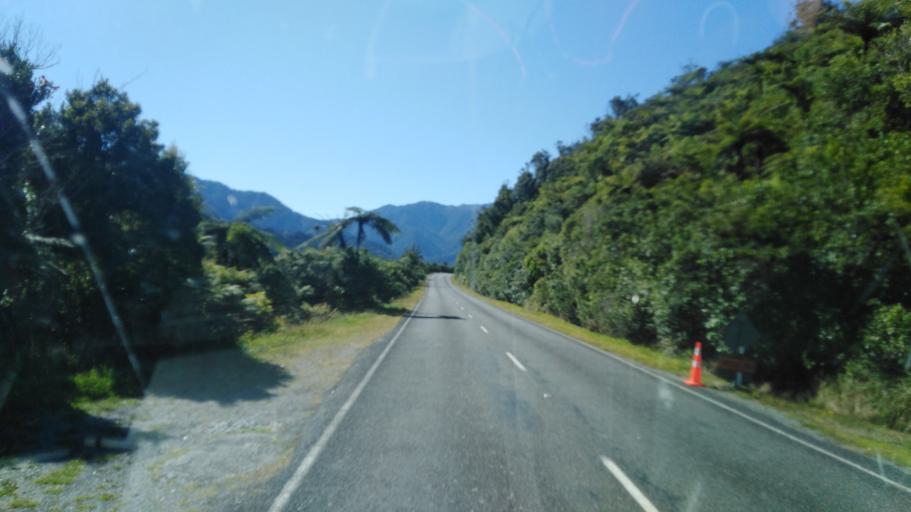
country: NZ
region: West Coast
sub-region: Buller District
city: Westport
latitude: -41.5307
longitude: 171.9501
